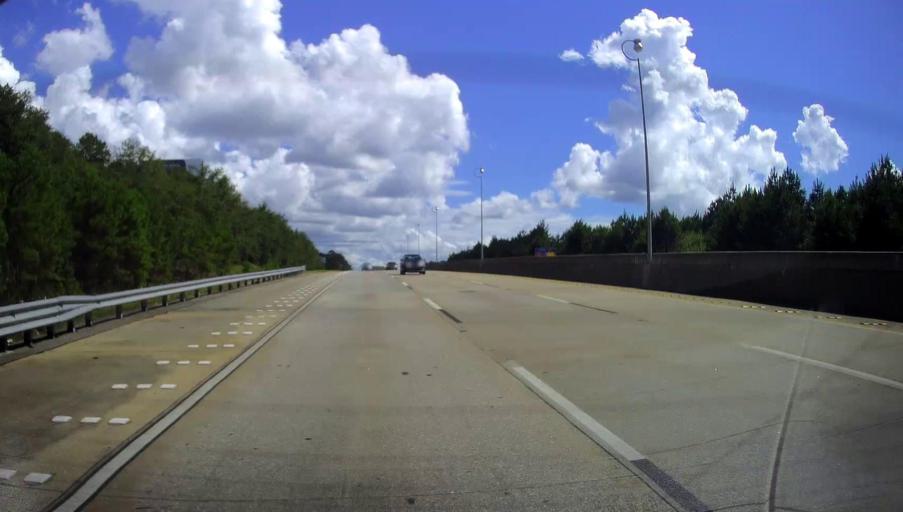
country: US
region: Georgia
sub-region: Muscogee County
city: Columbus
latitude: 32.4225
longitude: -84.9281
